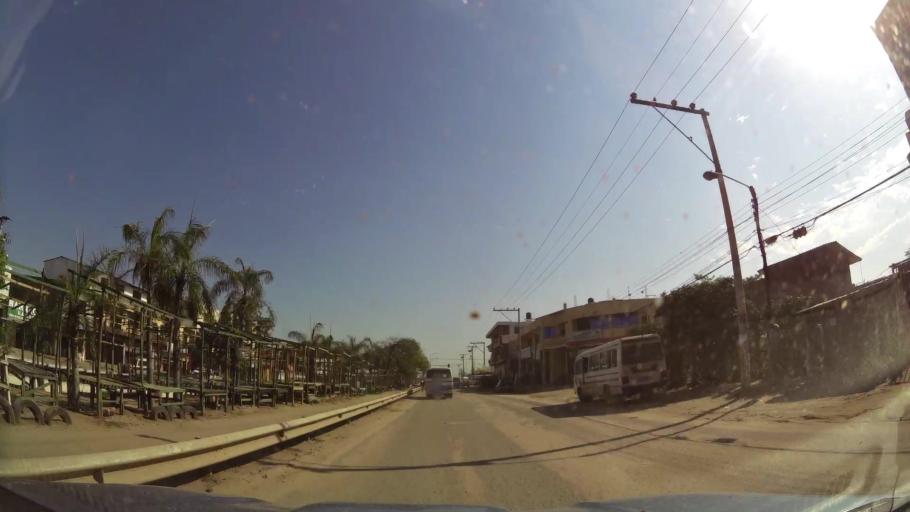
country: BO
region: Santa Cruz
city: Santa Cruz de la Sierra
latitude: -17.8281
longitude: -63.1379
